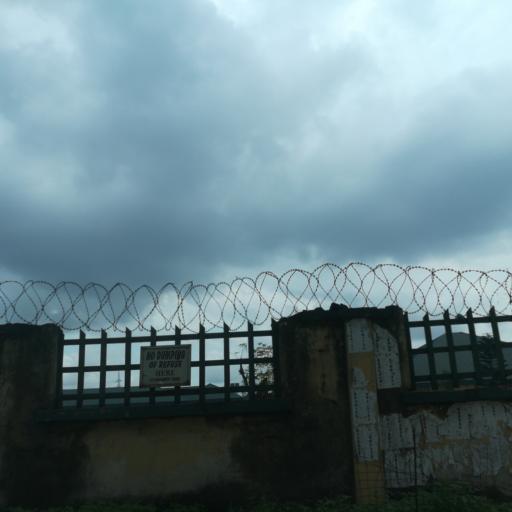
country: NG
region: Rivers
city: Port Harcourt
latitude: 4.8279
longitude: 7.0385
